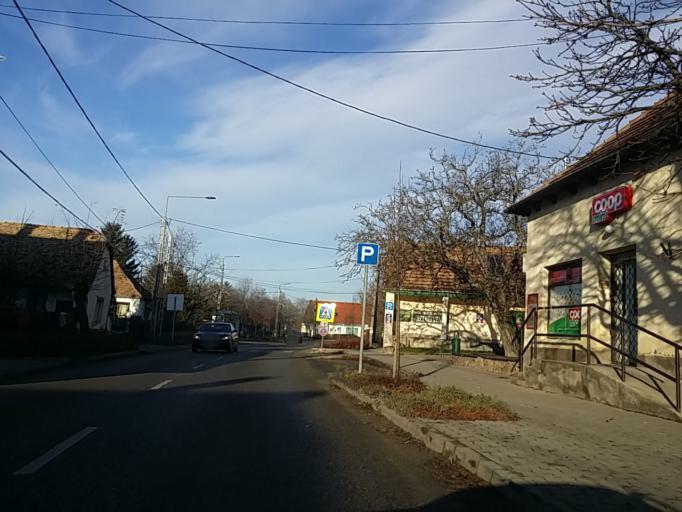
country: HU
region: Pest
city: Telki
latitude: 47.5460
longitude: 18.8300
